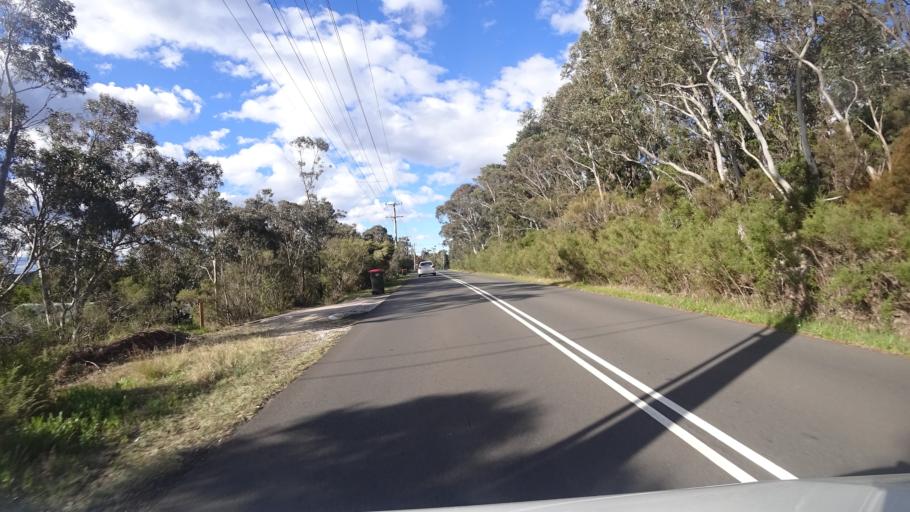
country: AU
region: New South Wales
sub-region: Blue Mountains Municipality
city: Katoomba
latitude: -33.7177
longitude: 150.2951
